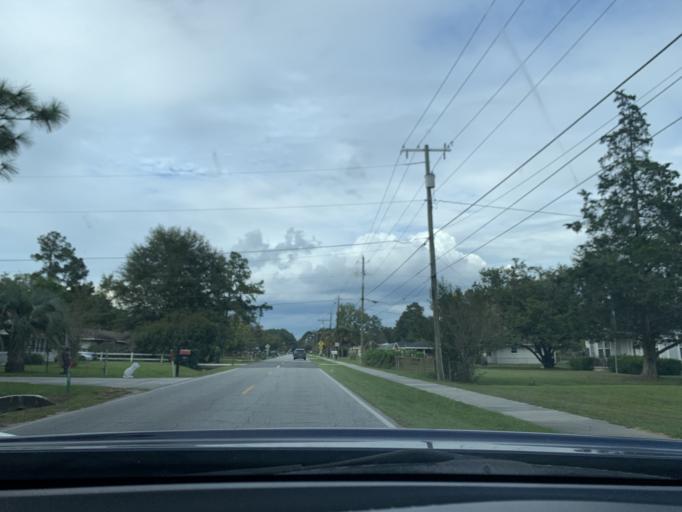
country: US
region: Georgia
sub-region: Chatham County
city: Pooler
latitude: 32.1023
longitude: -81.2536
